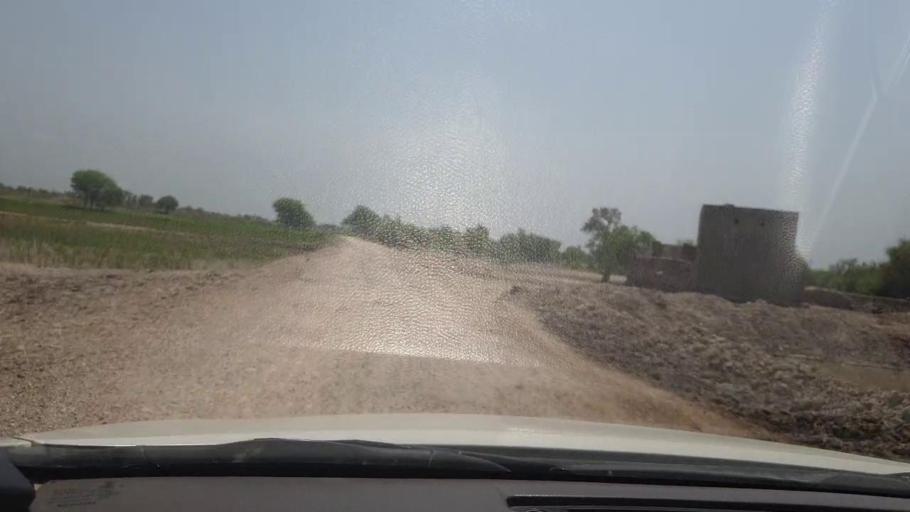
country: PK
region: Sindh
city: Garhi Yasin
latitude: 27.9206
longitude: 68.5528
